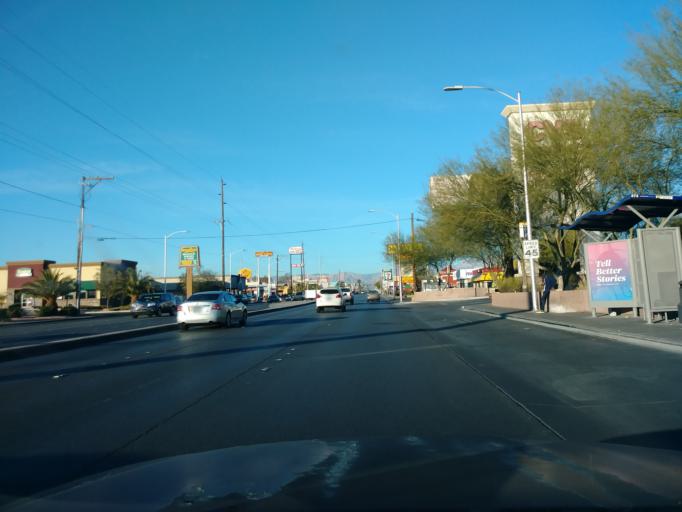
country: US
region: Nevada
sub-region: Clark County
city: Spring Valley
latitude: 36.1592
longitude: -115.2063
